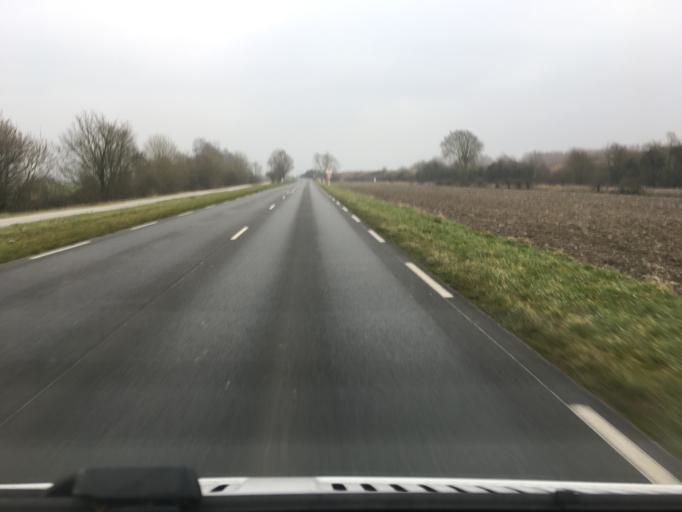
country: FR
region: Picardie
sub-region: Departement de la Somme
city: Le Crotoy
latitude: 50.2219
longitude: 1.6384
